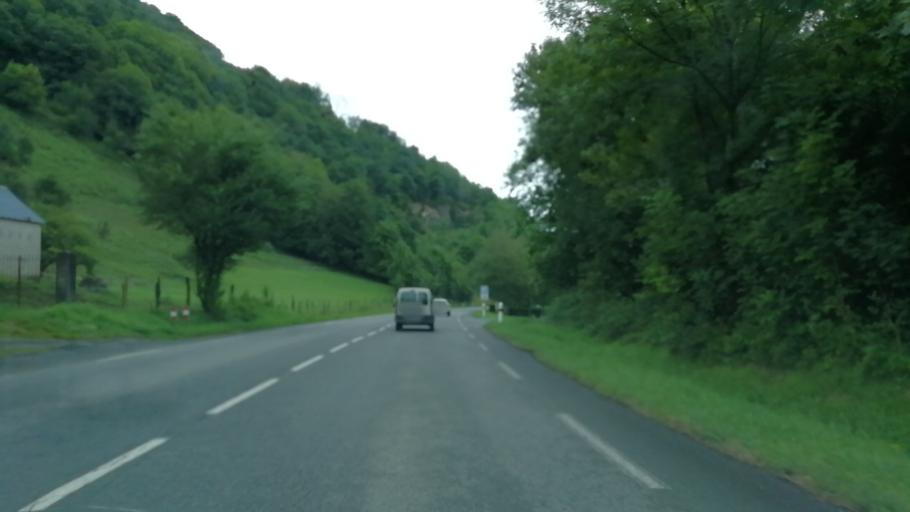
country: FR
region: Aquitaine
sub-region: Departement des Pyrenees-Atlantiques
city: Arette
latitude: 43.0969
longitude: -0.6225
